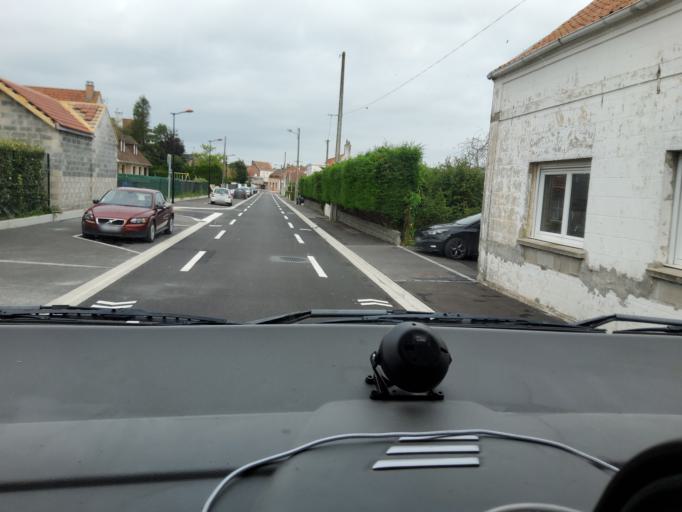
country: FR
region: Nord-Pas-de-Calais
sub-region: Departement du Pas-de-Calais
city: Audruicq
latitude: 50.8778
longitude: 2.0861
